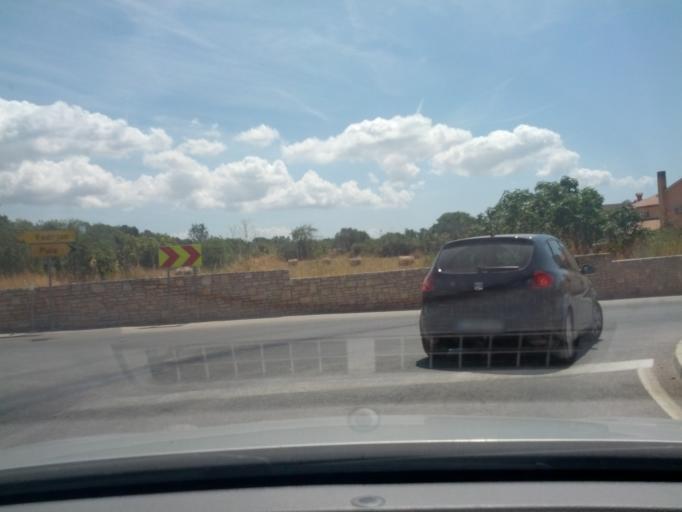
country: HR
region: Istarska
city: Fazana
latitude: 44.9322
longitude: 13.8058
